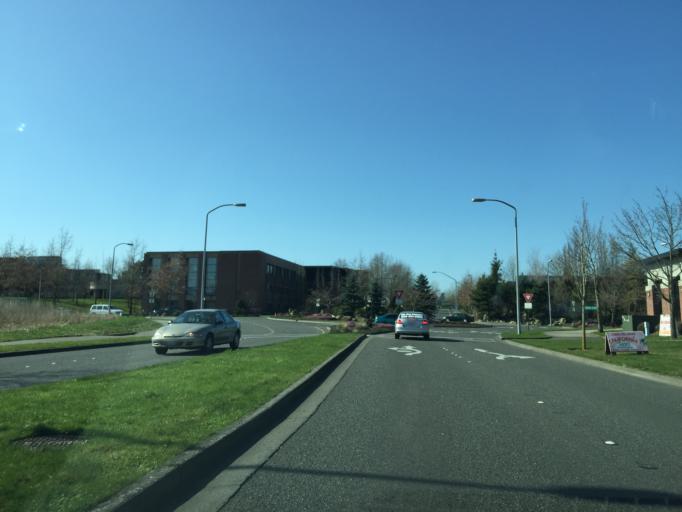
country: US
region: Washington
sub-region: Whatcom County
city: Bellingham
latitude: 48.7952
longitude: -122.4905
